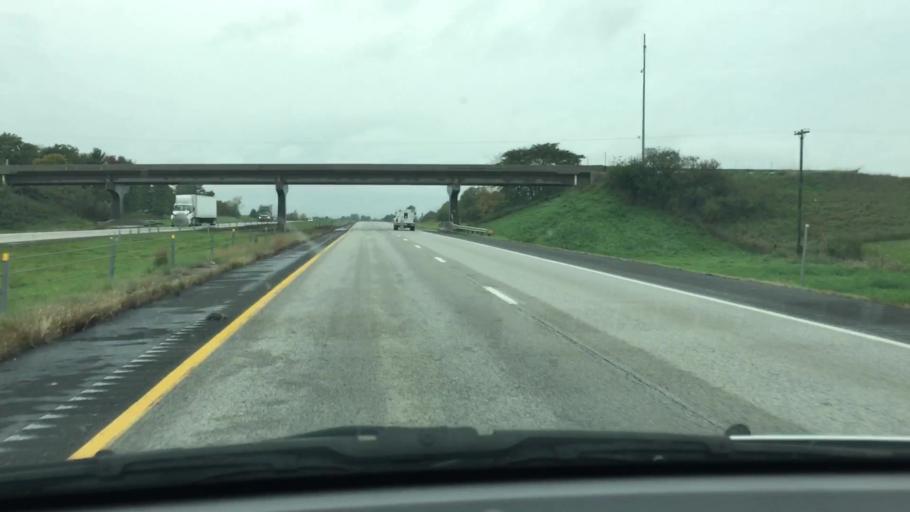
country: US
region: Iowa
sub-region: Johnson County
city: Tiffin
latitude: 41.6922
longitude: -91.7540
